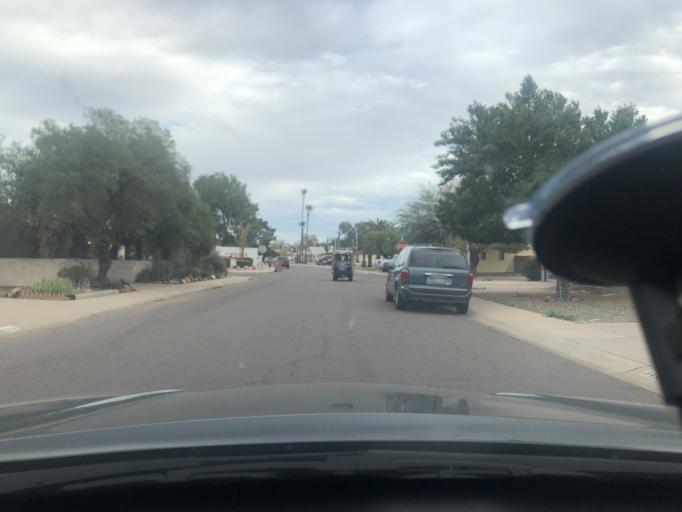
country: US
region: Arizona
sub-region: Maricopa County
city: Scottsdale
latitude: 33.4926
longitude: -111.8988
